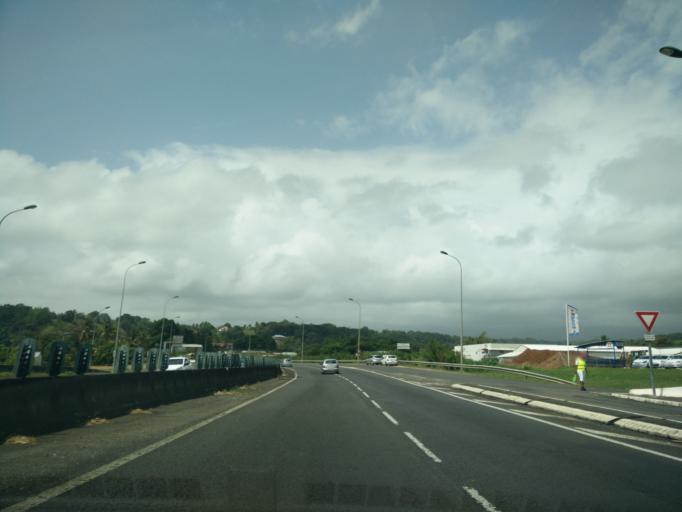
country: GP
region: Guadeloupe
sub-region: Guadeloupe
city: Petit-Bourg
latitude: 16.2021
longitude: -61.6058
